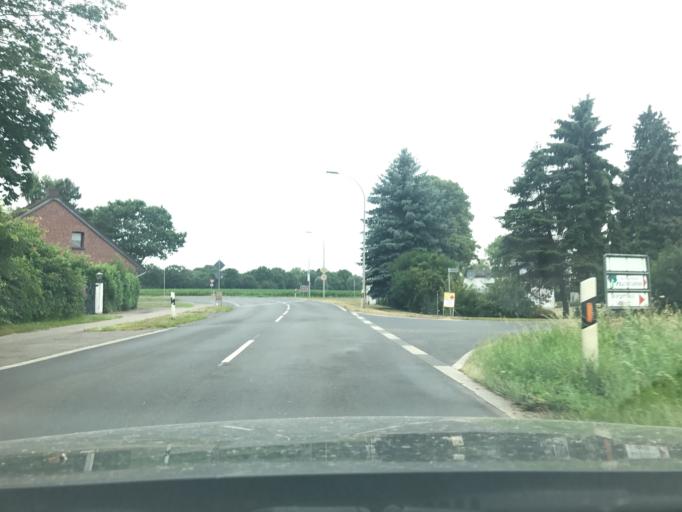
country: DE
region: North Rhine-Westphalia
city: Kempen
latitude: 51.3940
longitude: 6.4225
